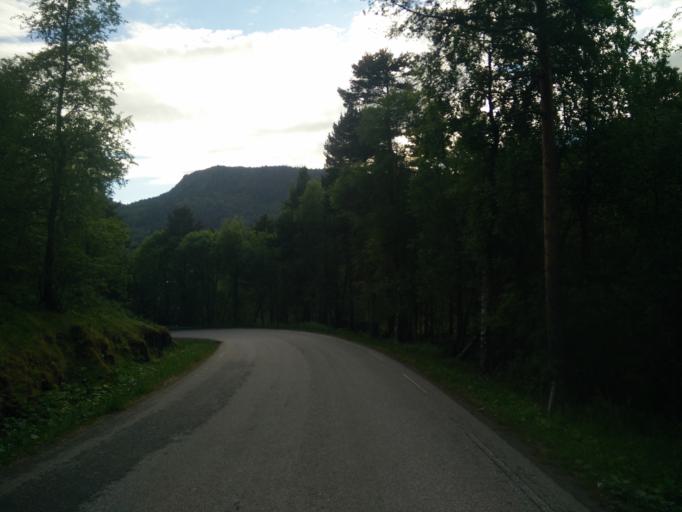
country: NO
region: More og Romsdal
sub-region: Kristiansund
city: Rensvik
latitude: 63.0201
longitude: 7.9605
